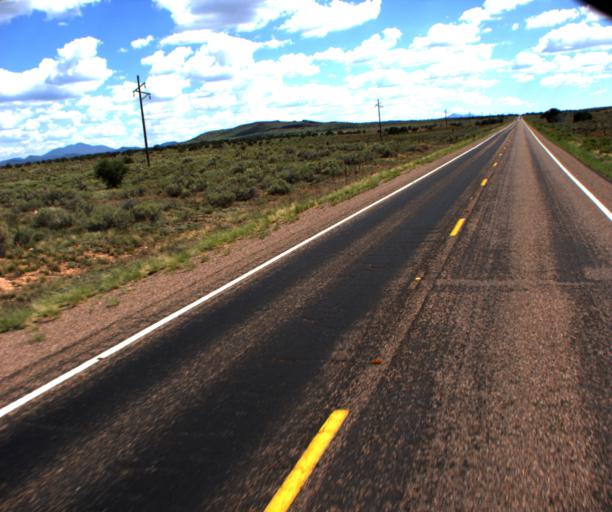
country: US
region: Arizona
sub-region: Coconino County
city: Williams
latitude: 35.5757
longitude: -112.1537
